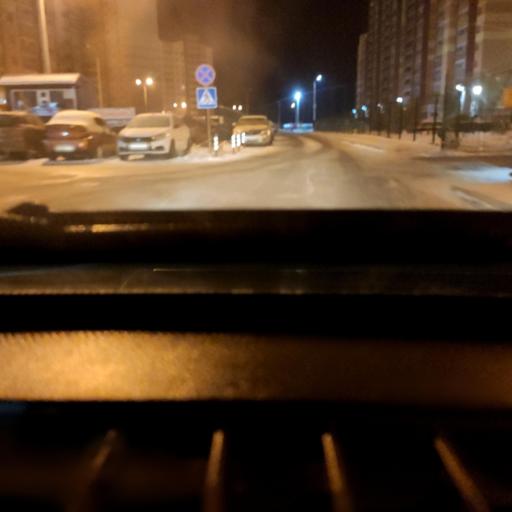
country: RU
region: Perm
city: Perm
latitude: 58.0841
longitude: 56.4045
